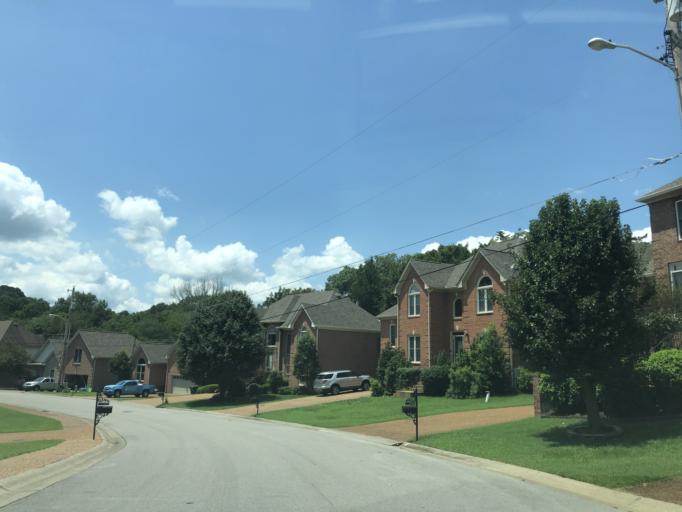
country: US
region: Tennessee
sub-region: Wilson County
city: Green Hill
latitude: 36.1932
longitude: -86.5903
